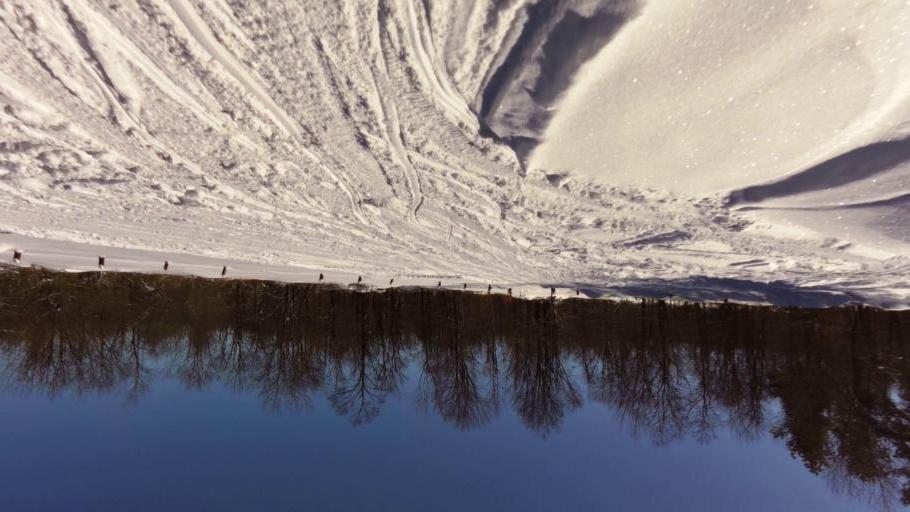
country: US
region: New York
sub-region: Chautauqua County
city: Fredonia
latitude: 42.3484
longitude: -79.1989
